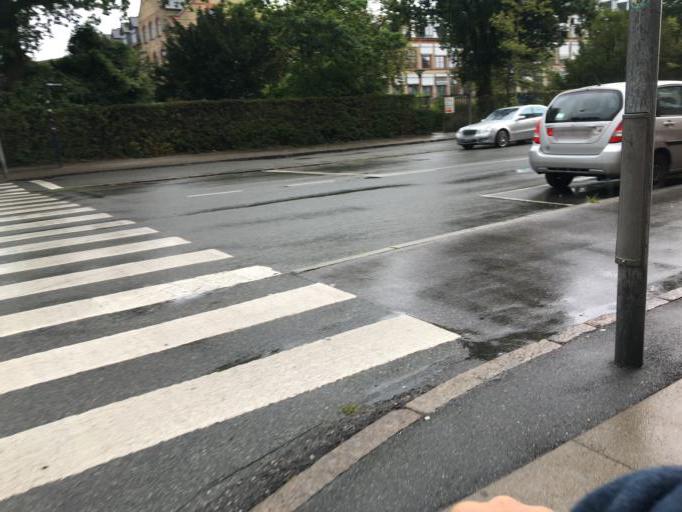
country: DK
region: Capital Region
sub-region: Tarnby Kommune
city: Tarnby
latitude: 55.6541
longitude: 12.6190
